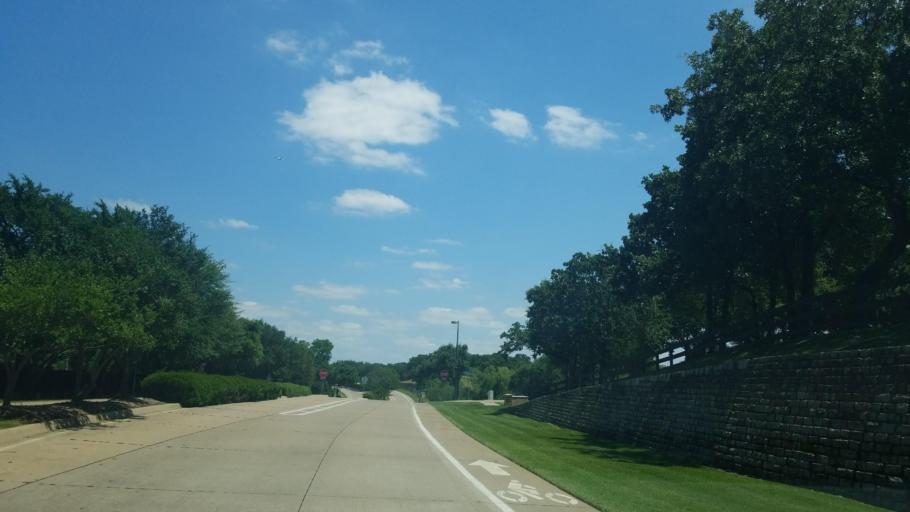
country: US
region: Texas
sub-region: Denton County
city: Copper Canyon
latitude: 33.0923
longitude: -97.0757
